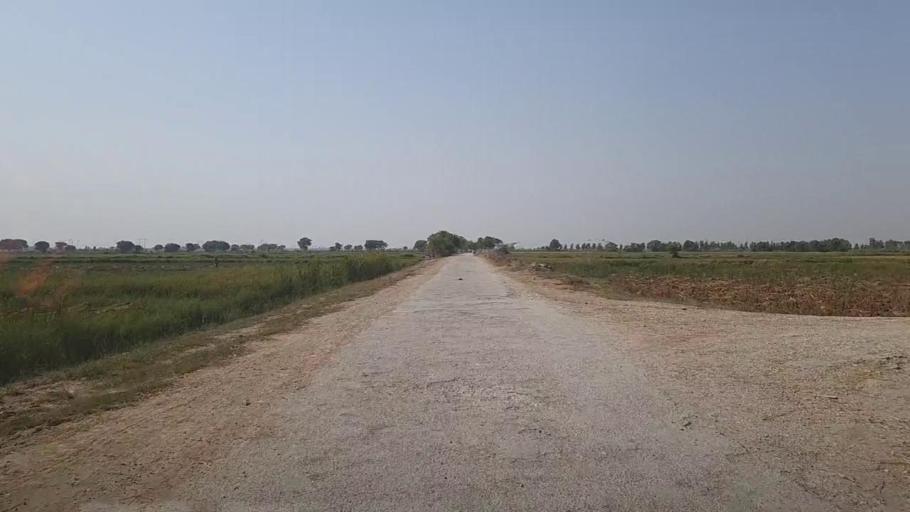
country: PK
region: Sindh
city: Kandhkot
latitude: 28.3941
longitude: 69.3192
